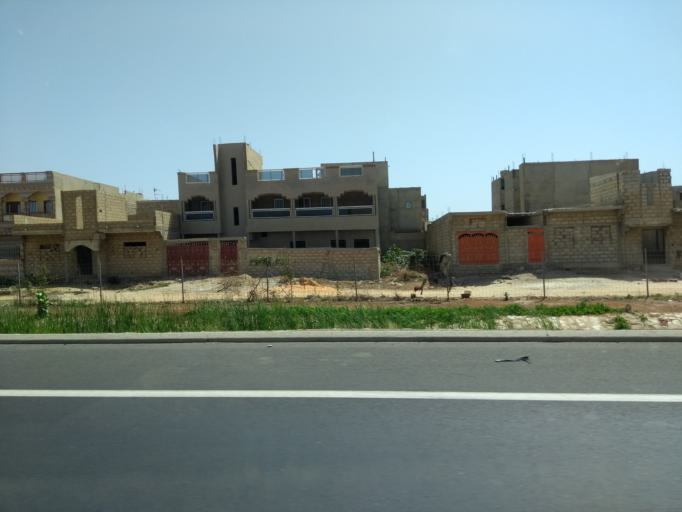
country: SN
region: Dakar
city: Pikine
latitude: 14.7518
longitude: -17.2982
